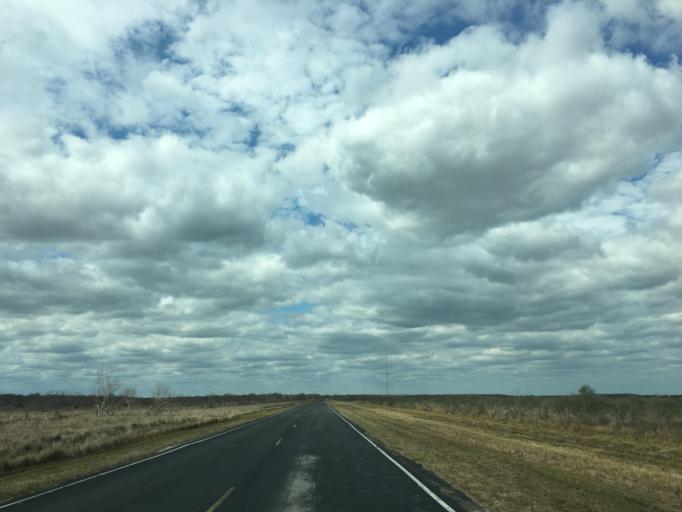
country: US
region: Texas
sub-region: Brazoria County
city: Oyster Creek
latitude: 29.0655
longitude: -95.2992
